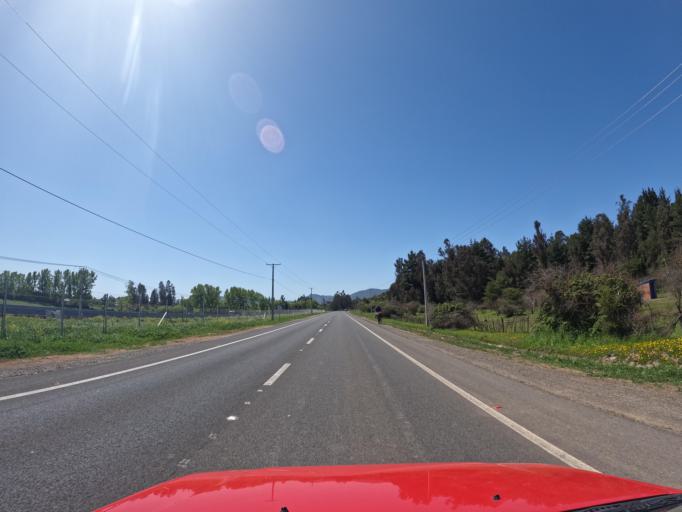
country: CL
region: Maule
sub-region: Provincia de Linares
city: Colbun
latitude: -35.7188
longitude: -71.4098
